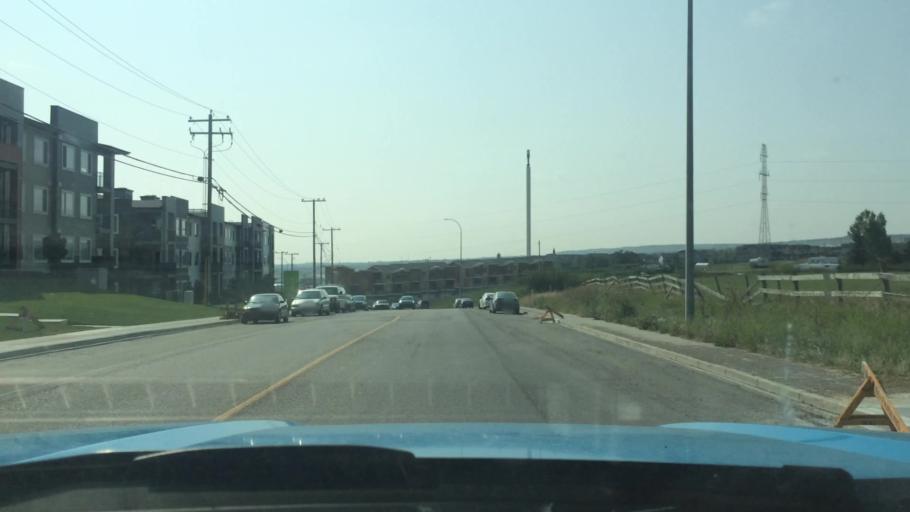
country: CA
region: Alberta
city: Calgary
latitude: 51.1711
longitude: -114.1374
